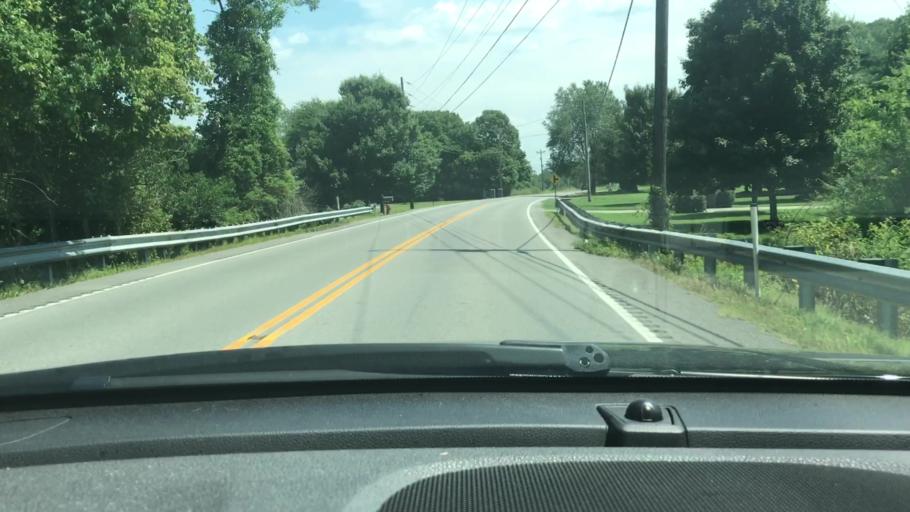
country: US
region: Tennessee
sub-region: Sumner County
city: Shackle Island
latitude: 36.4033
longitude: -86.6319
